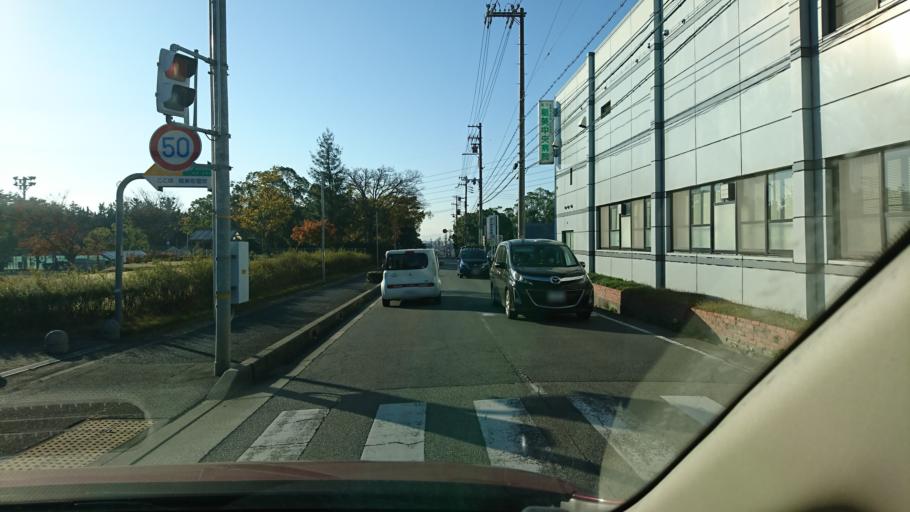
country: JP
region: Hyogo
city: Miki
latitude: 34.7508
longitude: 134.9208
